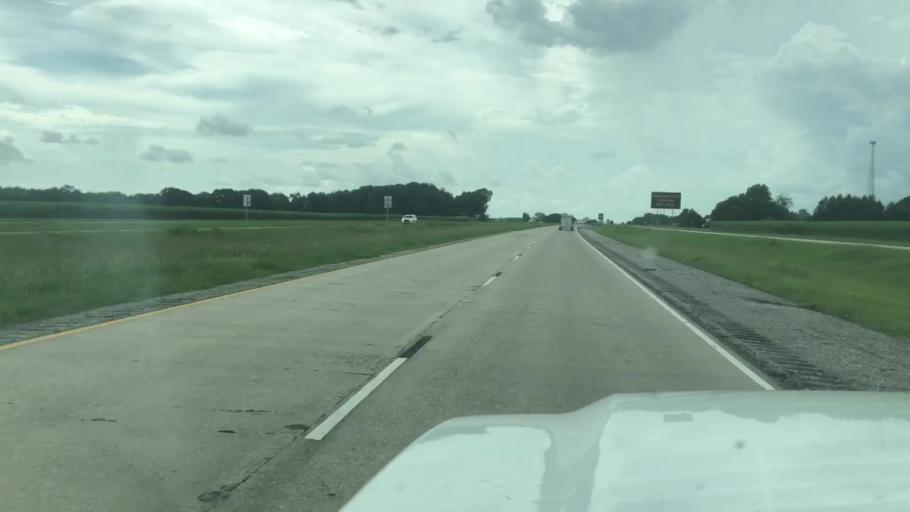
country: US
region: Louisiana
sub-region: Iberia Parish
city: Jeanerette
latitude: 29.8611
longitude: -91.6220
